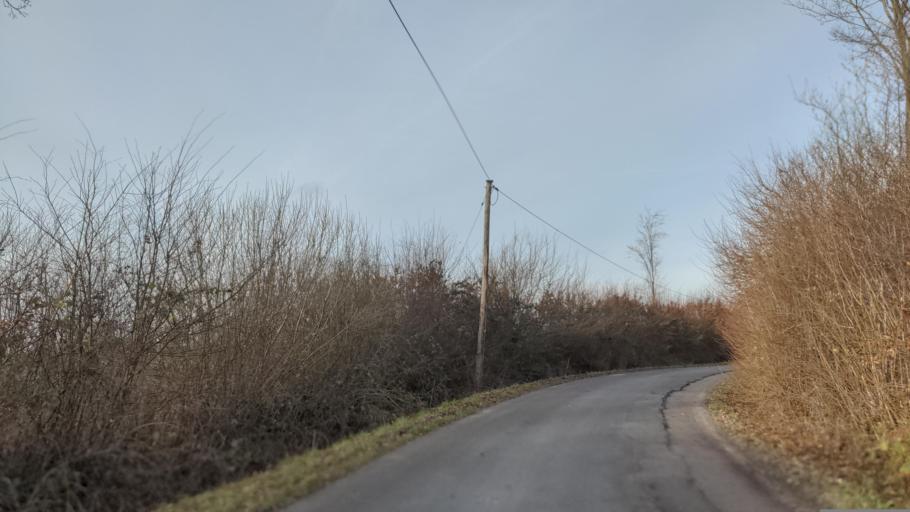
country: DE
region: Schleswig-Holstein
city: Eutin
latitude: 54.1638
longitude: 10.6284
